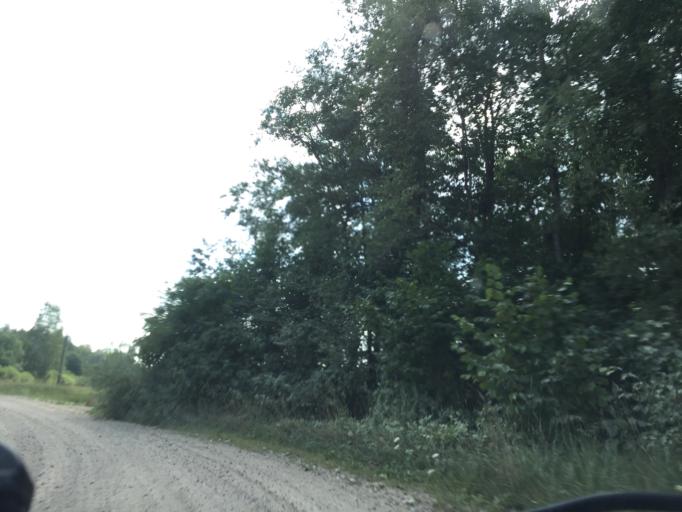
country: LT
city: Zagare
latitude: 56.3597
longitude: 23.1600
